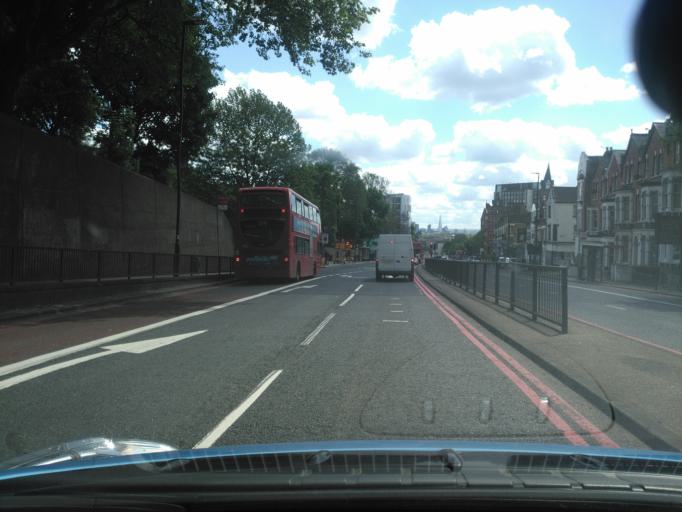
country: GB
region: England
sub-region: Greater London
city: Crouch End
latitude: 51.5696
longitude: -0.1373
